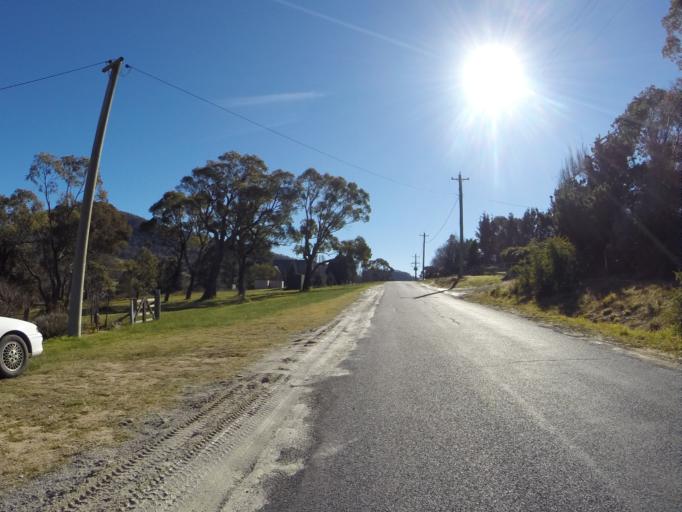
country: AU
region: New South Wales
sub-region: Oberon
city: Oberon
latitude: -33.5279
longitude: 149.9040
